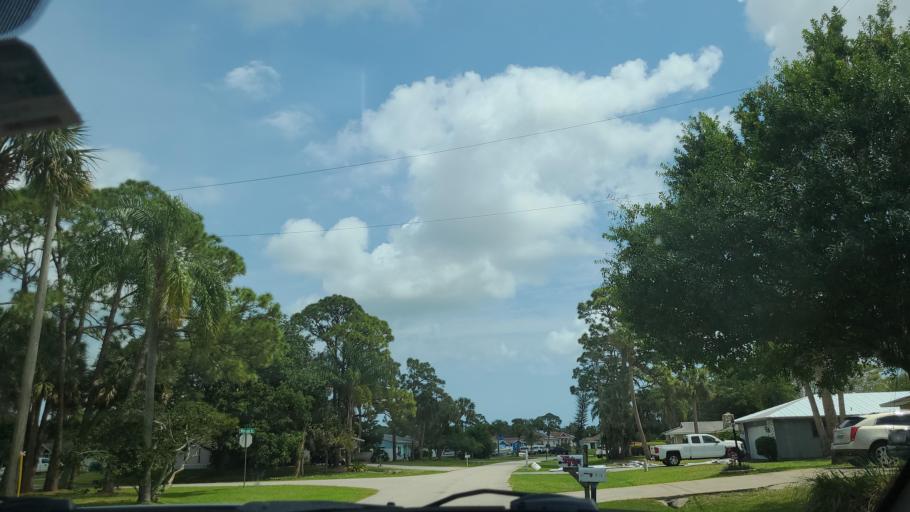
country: US
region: Florida
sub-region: Indian River County
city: Sebastian
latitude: 27.7974
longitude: -80.4897
